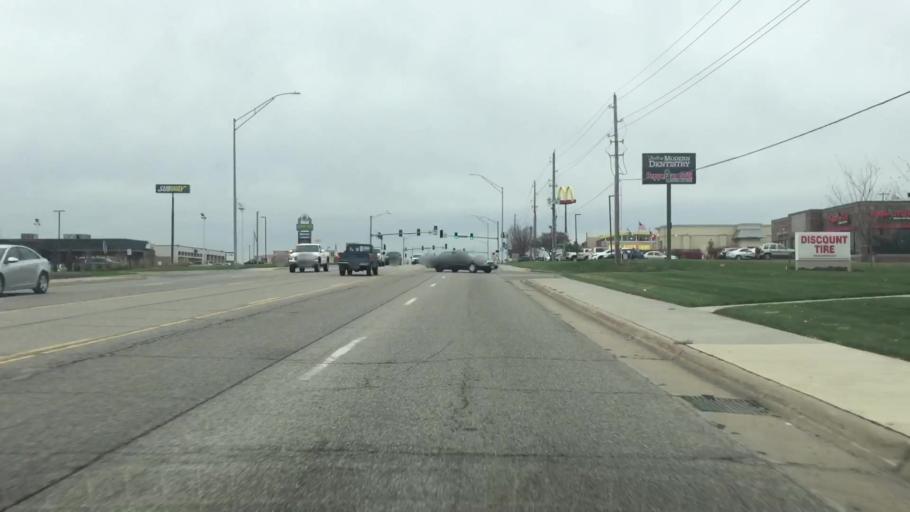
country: US
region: Missouri
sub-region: Cass County
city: Belton
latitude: 38.8134
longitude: -94.5093
